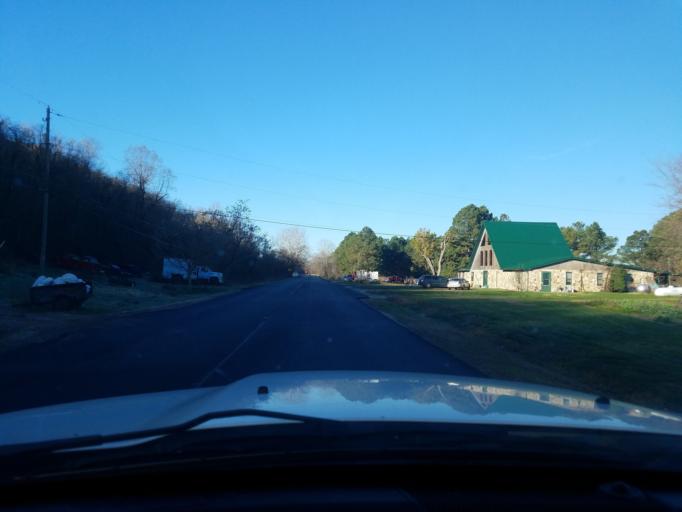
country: US
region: West Virginia
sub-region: Jackson County
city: Ravenswood
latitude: 38.8832
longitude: -81.8524
